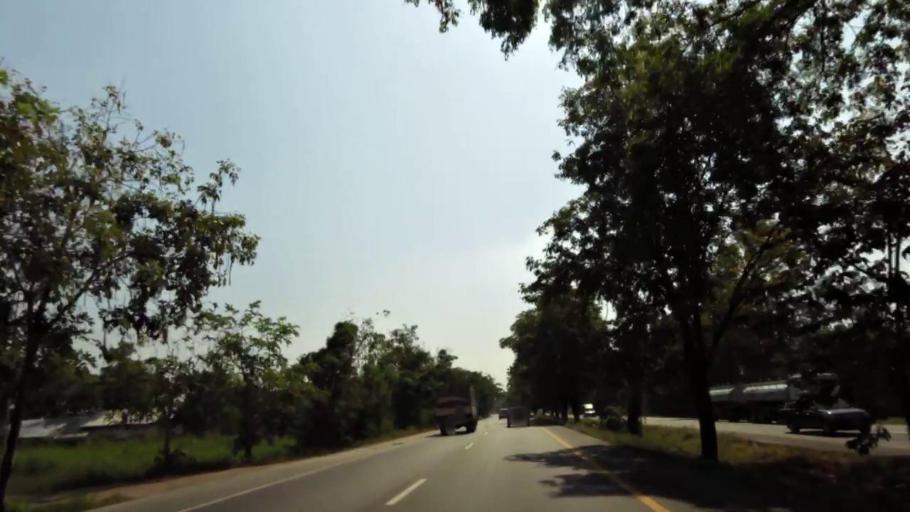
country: TH
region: Phichit
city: Bueng Na Rang
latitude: 16.0231
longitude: 100.1146
